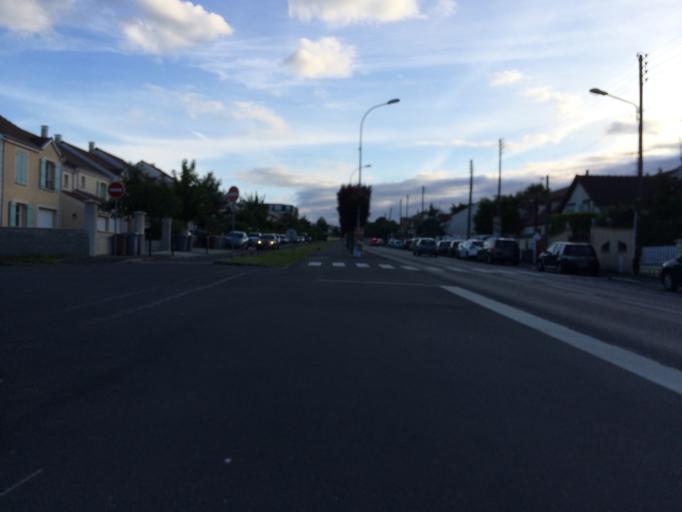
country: FR
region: Ile-de-France
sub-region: Departement de l'Essonne
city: Montgeron
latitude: 48.6918
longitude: 2.4432
